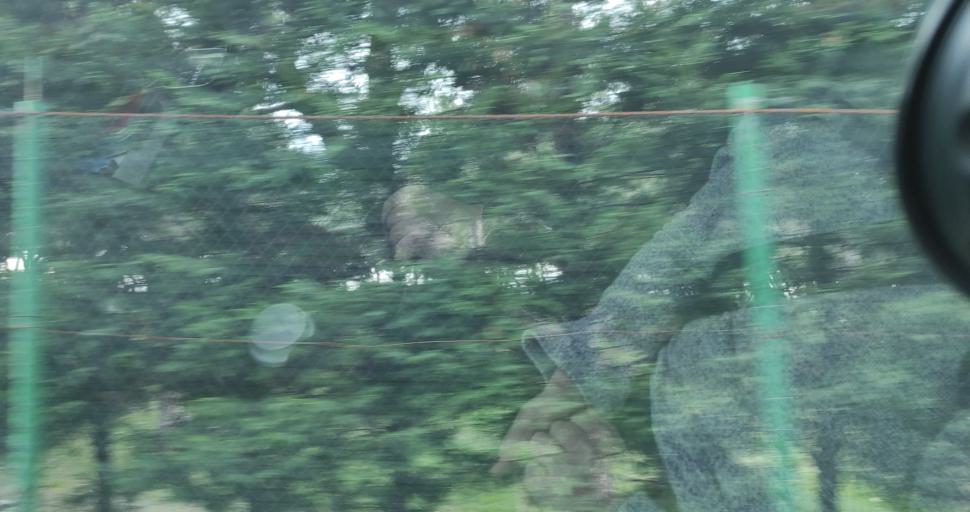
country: AL
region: Lezhe
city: Shengjin
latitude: 41.8191
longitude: 19.5651
